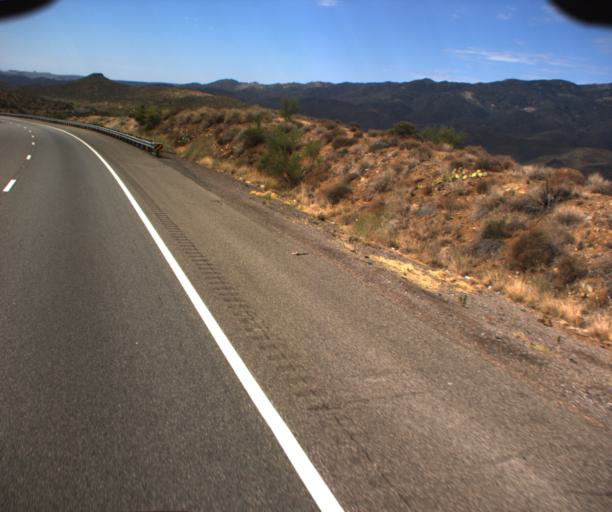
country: US
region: Arizona
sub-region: Yavapai County
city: Black Canyon City
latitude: 34.1584
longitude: -112.1463
